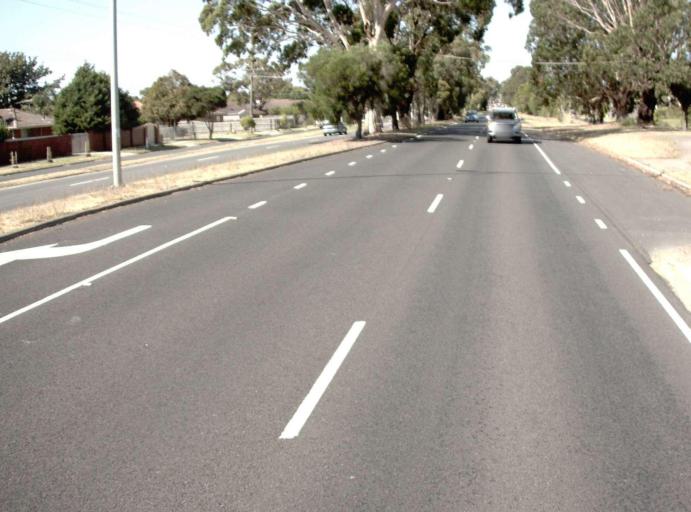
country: AU
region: Victoria
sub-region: Frankston
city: Frankston North
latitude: -38.1174
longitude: 145.1506
